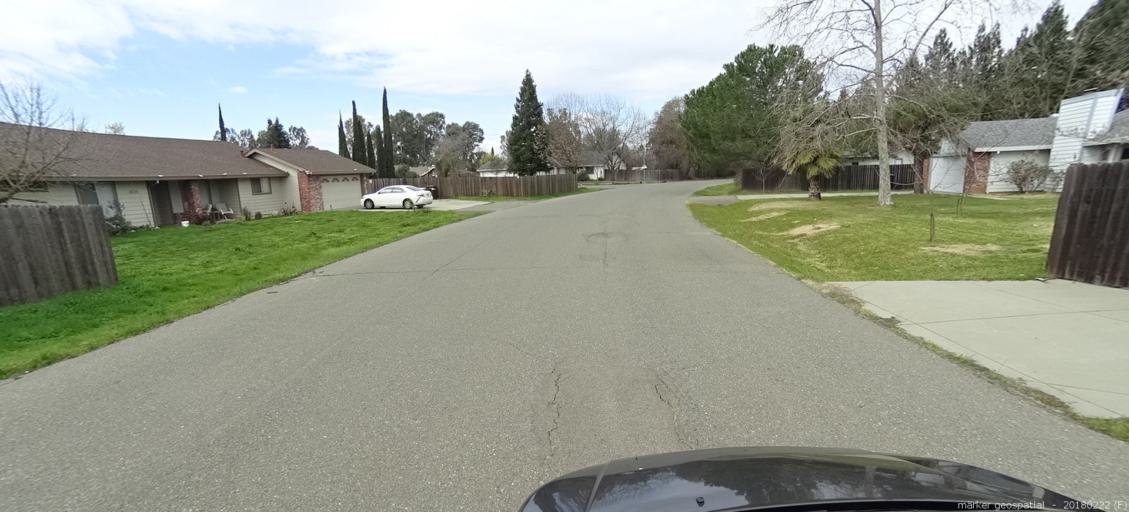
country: US
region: California
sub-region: Sacramento County
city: Rio Linda
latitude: 38.7180
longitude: -121.4131
